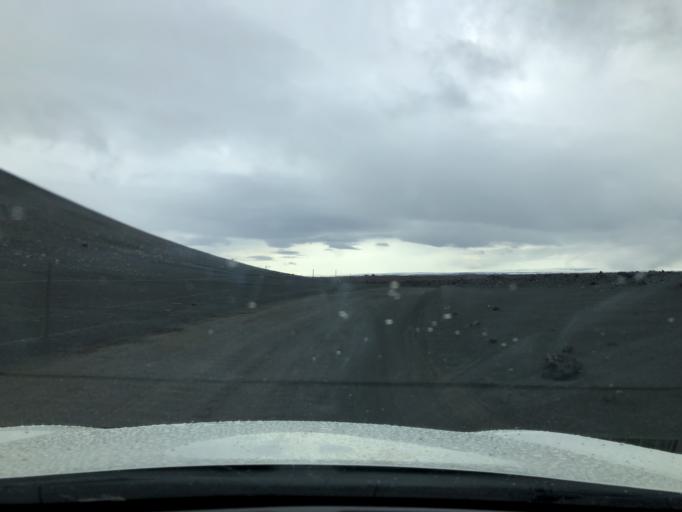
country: IS
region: Northeast
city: Laugar
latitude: 65.6111
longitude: -16.8808
